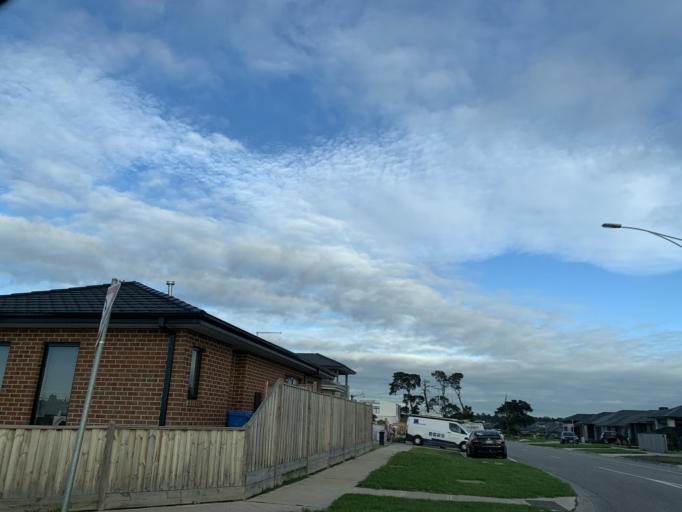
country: AU
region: Victoria
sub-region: Casey
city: Junction Village
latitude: -38.1290
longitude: 145.3078
